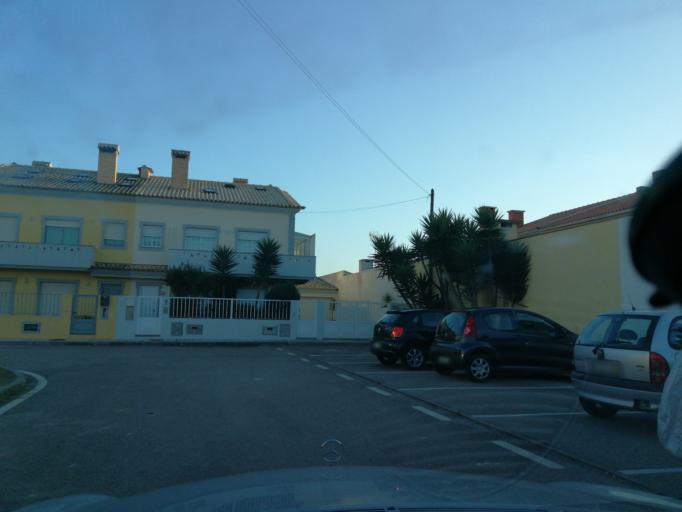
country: PT
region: Aveiro
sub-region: Murtosa
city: Murtosa
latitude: 40.7583
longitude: -8.7094
